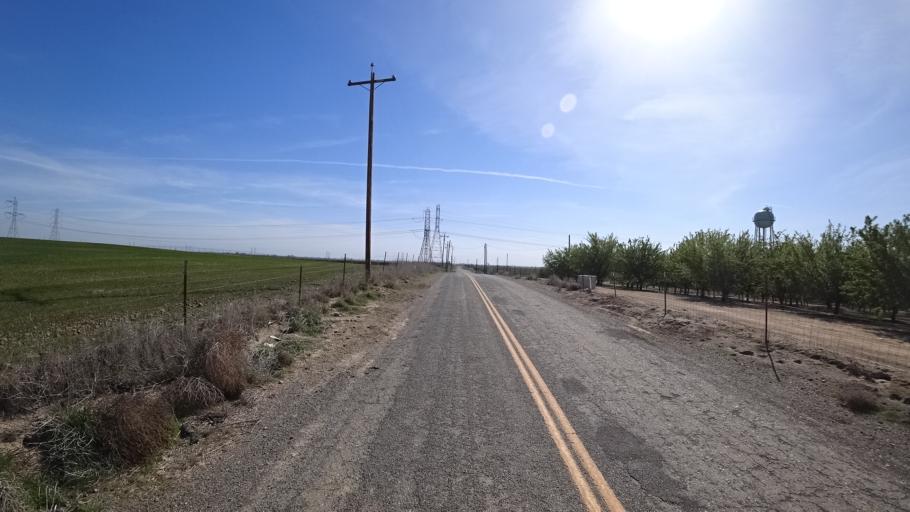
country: US
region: California
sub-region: Glenn County
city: Willows
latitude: 39.6116
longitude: -122.2762
